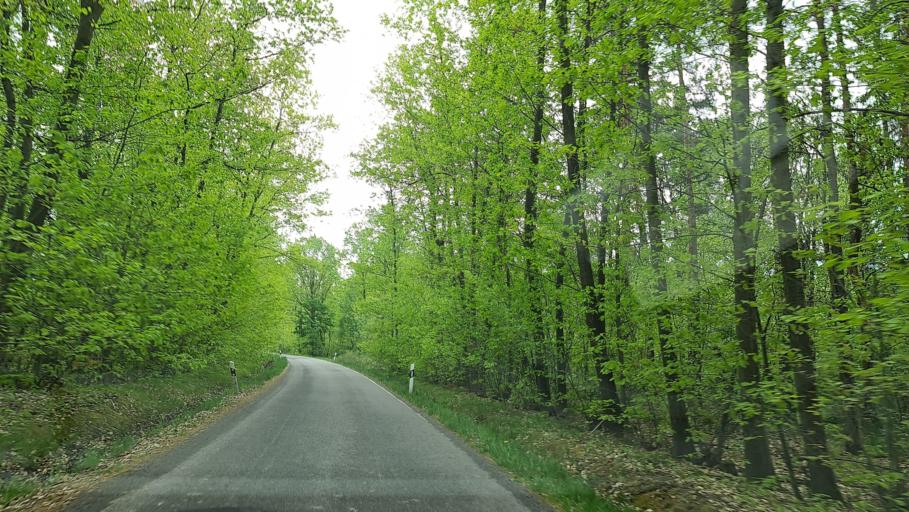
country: DE
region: Saxony
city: Hilbersdorf
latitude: 50.8435
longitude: 12.9863
